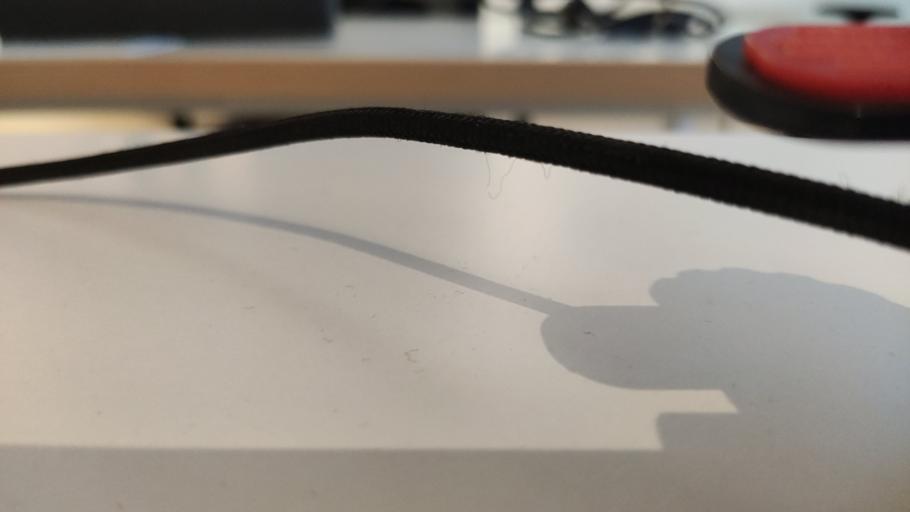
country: RU
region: Moskovskaya
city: Sychevo
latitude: 55.8362
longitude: 36.3291
